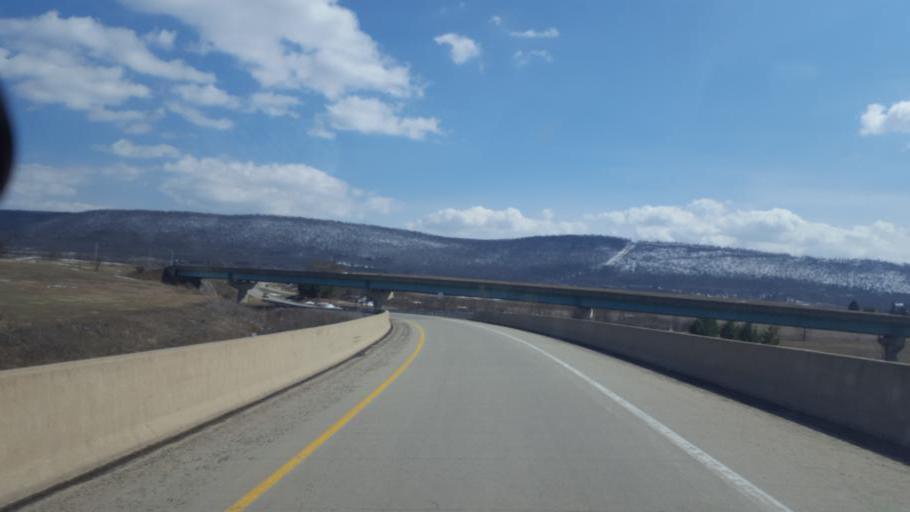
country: US
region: Pennsylvania
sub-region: Centre County
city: Pleasant Gap
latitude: 40.8904
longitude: -77.7336
